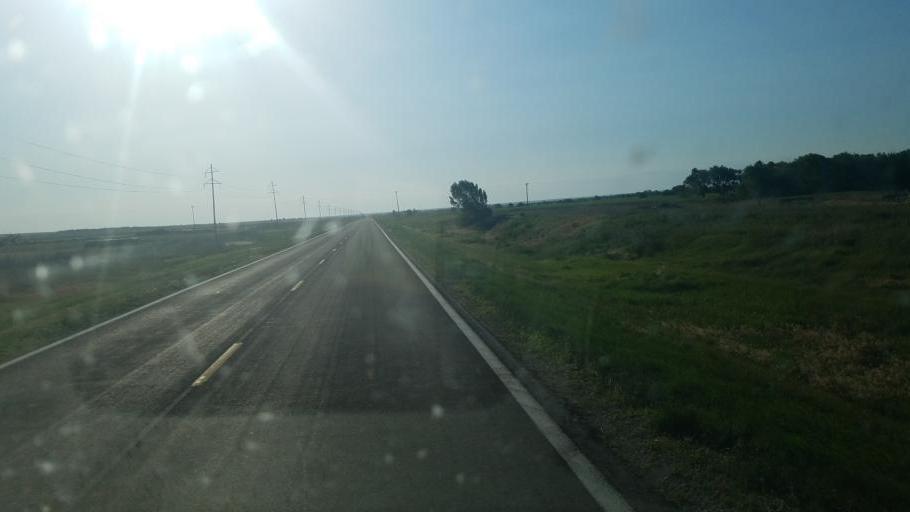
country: US
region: Kansas
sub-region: Hodgeman County
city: Jetmore
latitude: 38.0934
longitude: -99.8103
